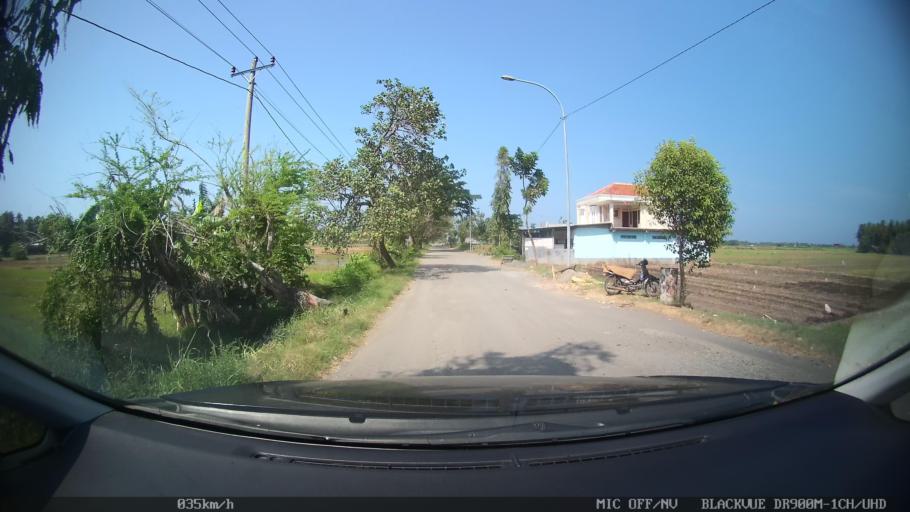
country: ID
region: Daerah Istimewa Yogyakarta
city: Srandakan
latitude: -7.9632
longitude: 110.2142
